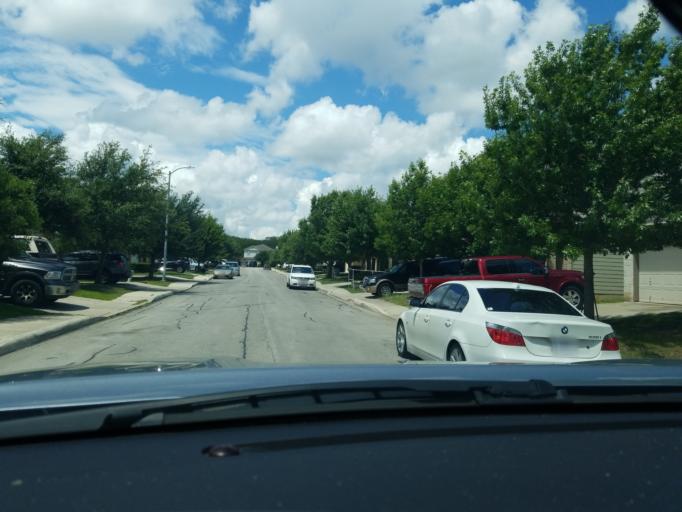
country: US
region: Texas
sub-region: Bexar County
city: Timberwood Park
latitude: 29.7018
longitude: -98.4831
